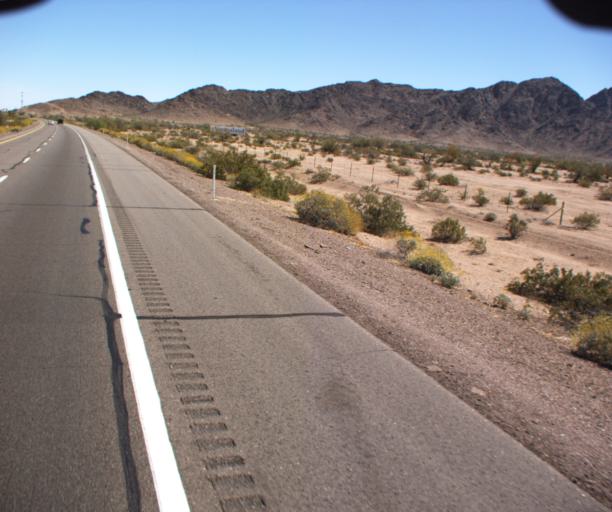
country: US
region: Arizona
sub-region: Yuma County
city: Wellton
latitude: 32.7221
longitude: -113.7640
